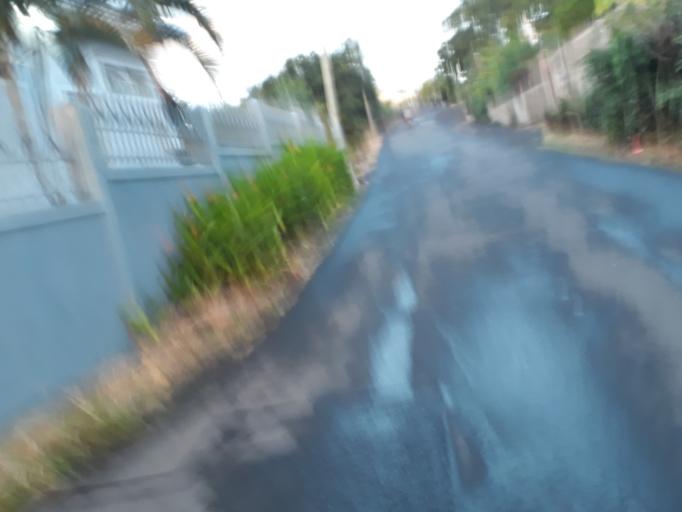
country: MU
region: Riviere du Rempart
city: Grand Baie
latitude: -20.0172
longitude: 57.5840
